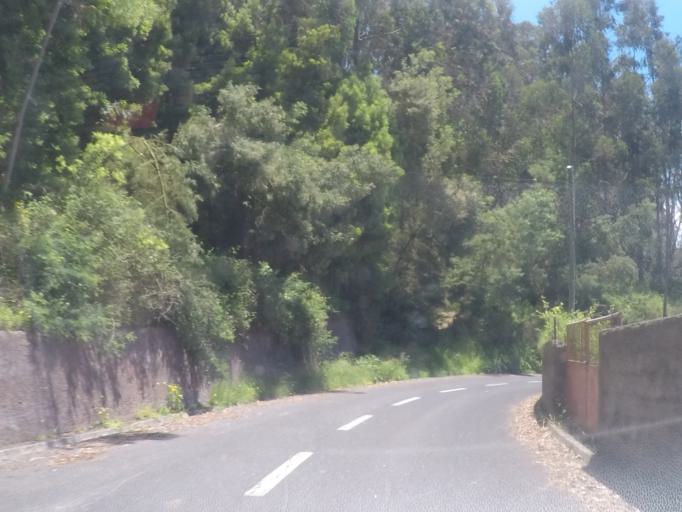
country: PT
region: Madeira
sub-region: Camara de Lobos
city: Curral das Freiras
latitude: 32.6911
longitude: -16.9750
